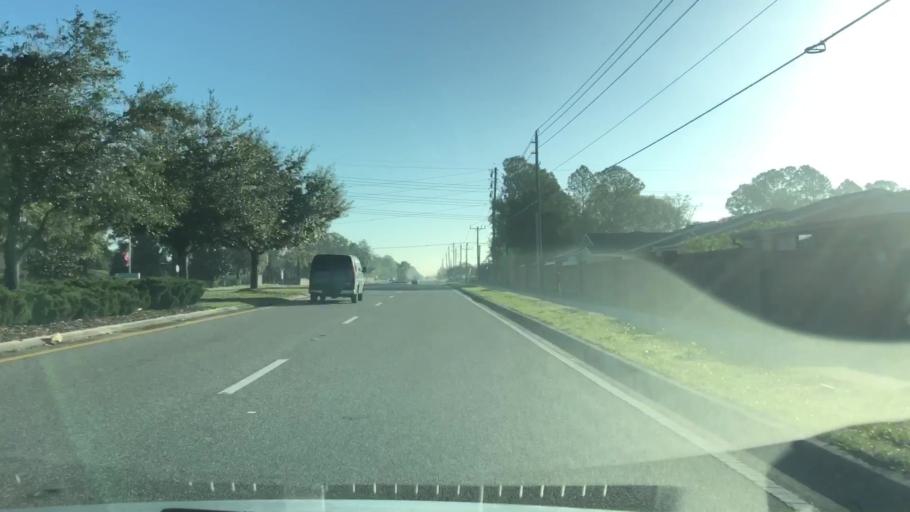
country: US
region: Florida
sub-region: Seminole County
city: Lake Mary
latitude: 28.7864
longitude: -81.3250
